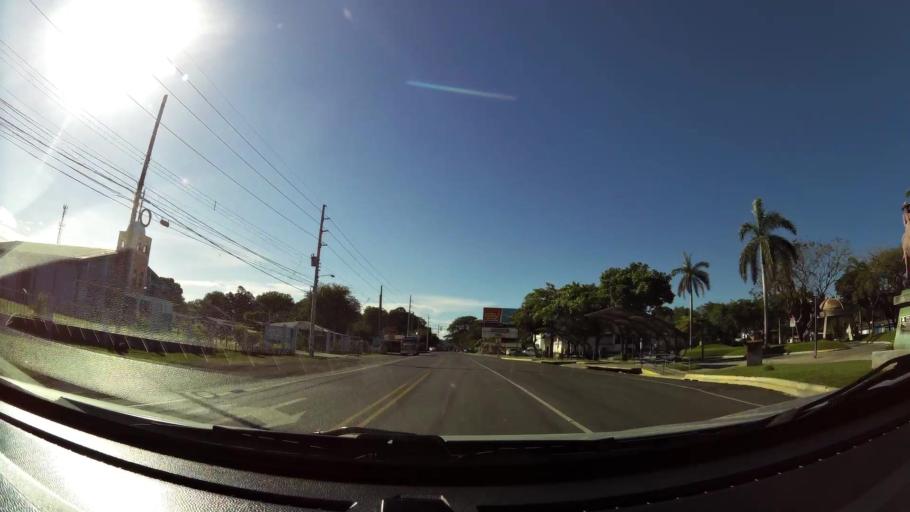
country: CR
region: Guanacaste
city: Belen
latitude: 10.4080
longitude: -85.5873
